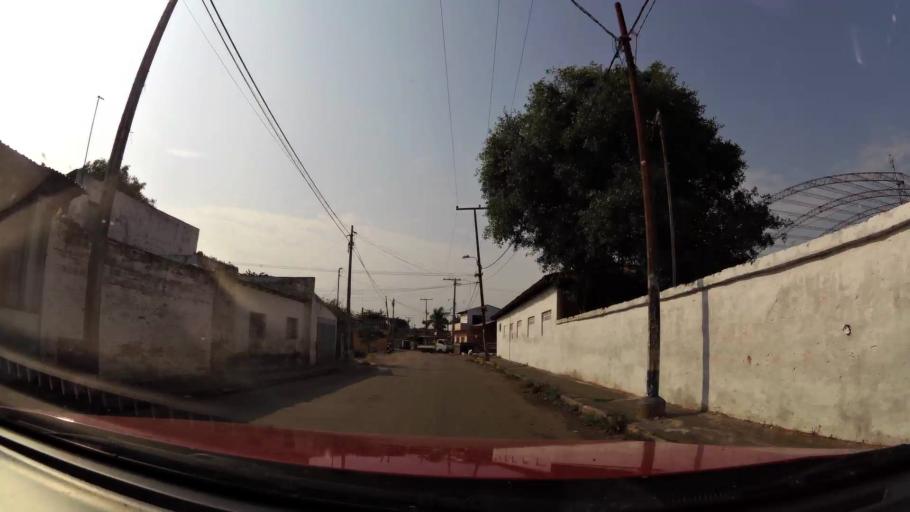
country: PY
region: Asuncion
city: Asuncion
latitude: -25.3005
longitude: -57.6657
